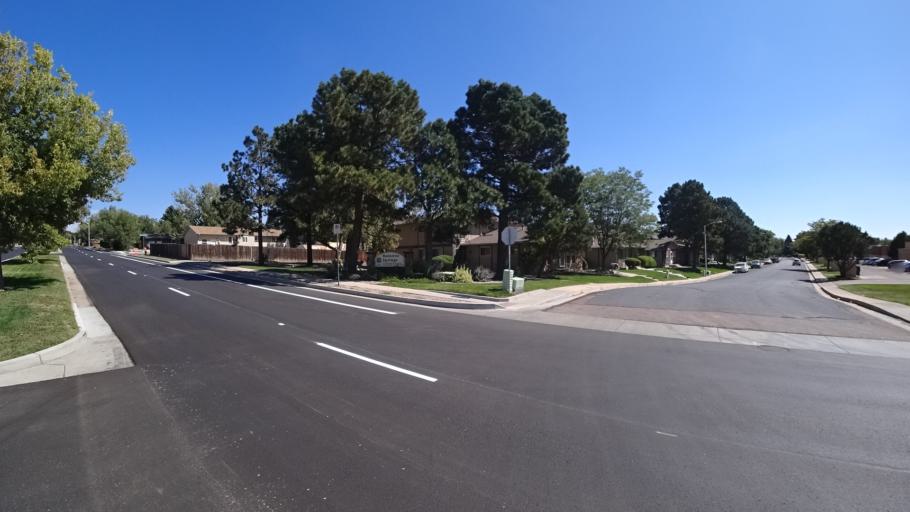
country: US
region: Colorado
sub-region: El Paso County
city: Cimarron Hills
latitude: 38.9028
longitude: -104.7670
